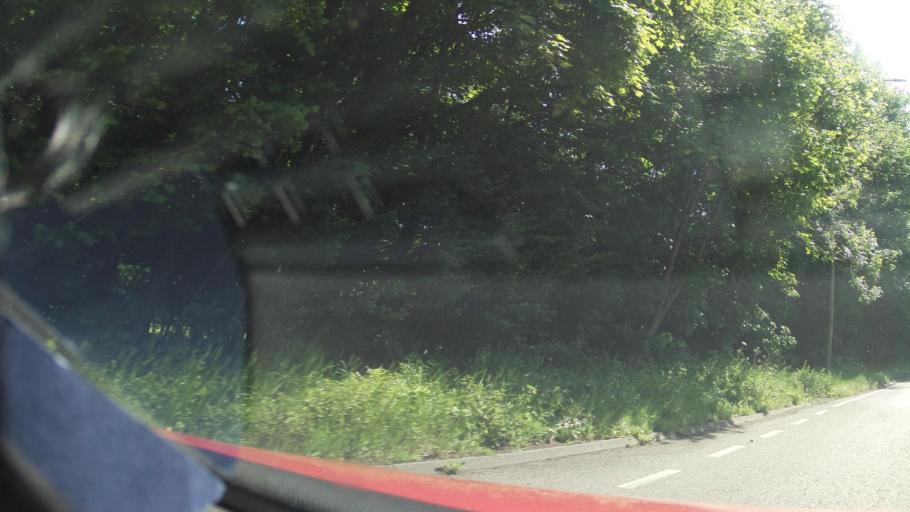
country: GB
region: England
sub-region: North Lincolnshire
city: Broughton
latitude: 53.5521
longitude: -0.5723
